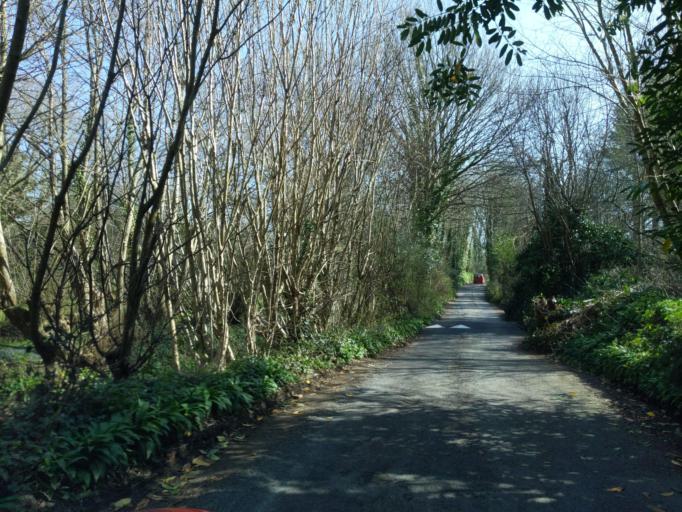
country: GB
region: England
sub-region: Devon
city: Plympton
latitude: 50.3845
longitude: -4.0502
